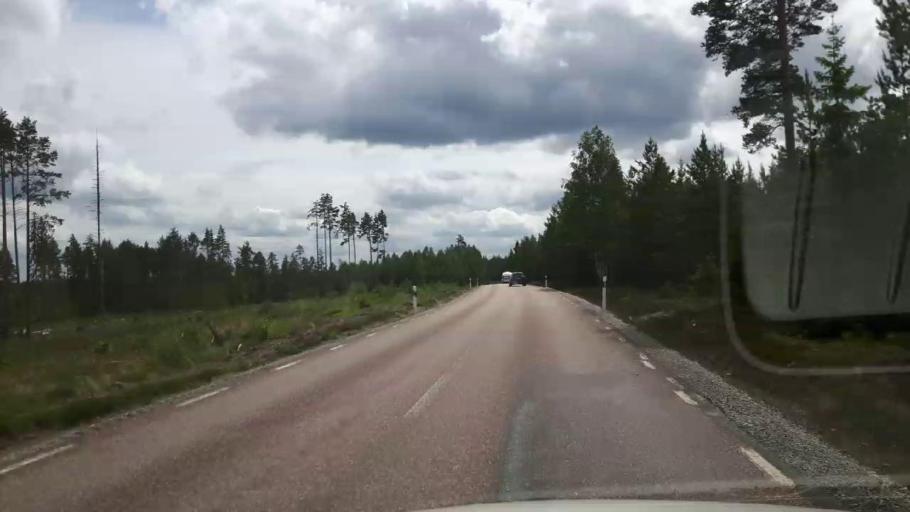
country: SE
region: Vaestmanland
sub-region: Skinnskattebergs Kommun
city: Skinnskatteberg
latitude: 59.8235
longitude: 15.8361
